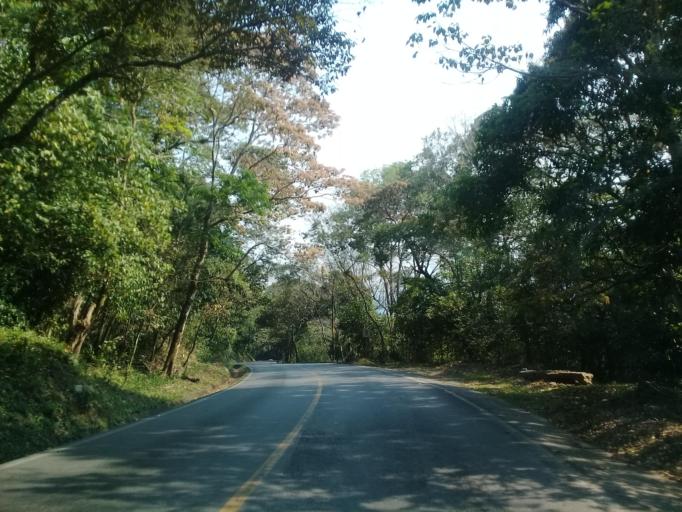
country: MX
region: Veracruz
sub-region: Ixtaczoquitlan
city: Campo Chico
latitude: 18.8421
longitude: -97.0283
